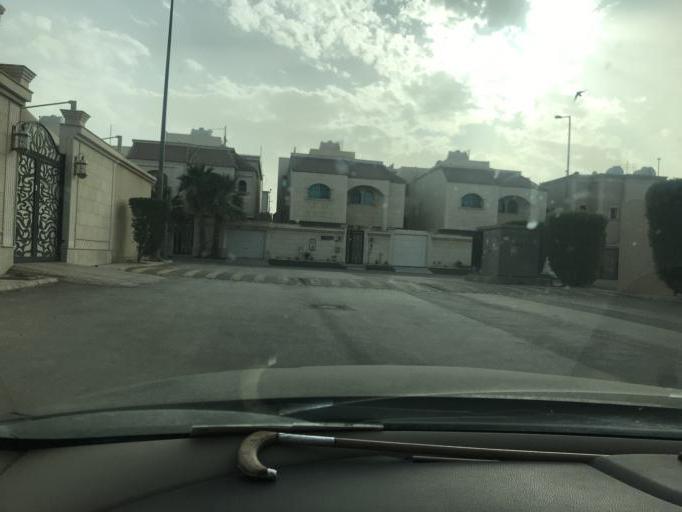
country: SA
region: Ar Riyad
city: Riyadh
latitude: 24.7805
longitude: 46.7134
